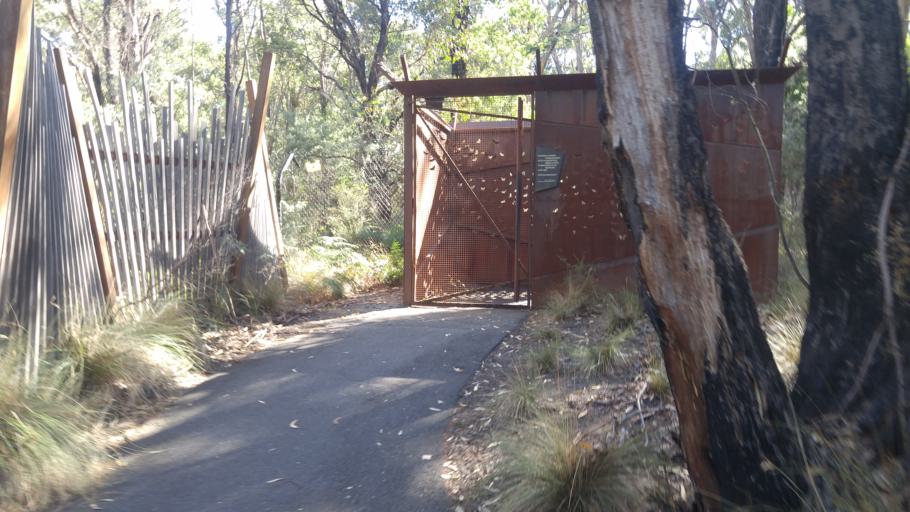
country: AU
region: Australian Capital Territory
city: Macarthur
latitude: -35.4668
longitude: 148.9047
